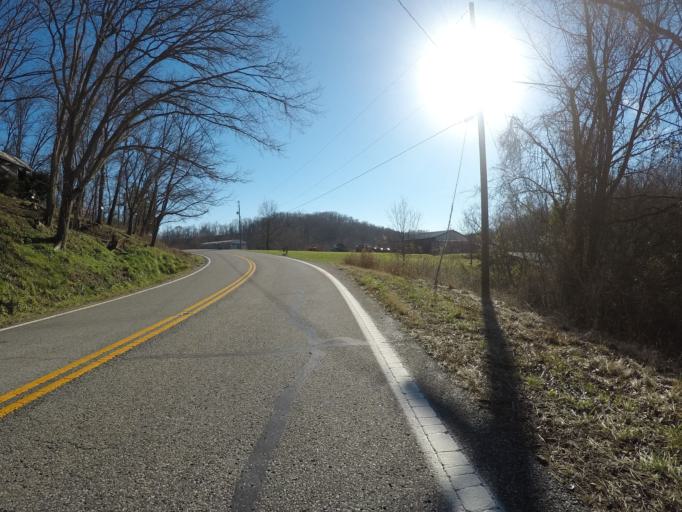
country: US
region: West Virginia
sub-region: Cabell County
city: Huntington
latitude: 38.4841
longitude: -82.4597
